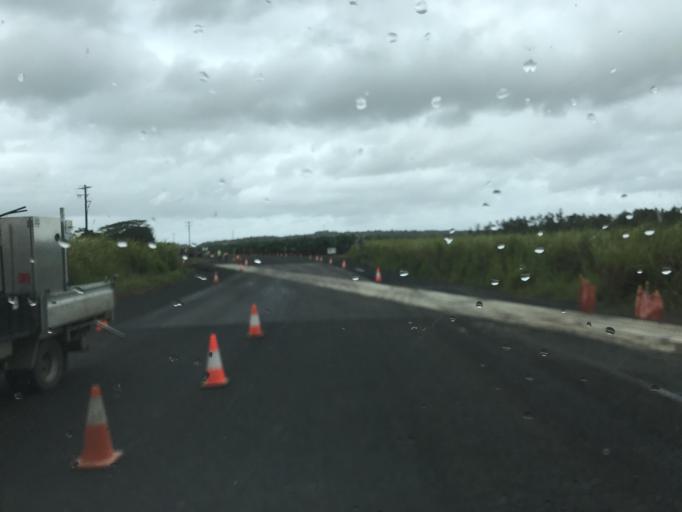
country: AU
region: Queensland
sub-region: Cassowary Coast
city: Innisfail
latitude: -17.5008
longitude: 145.9834
